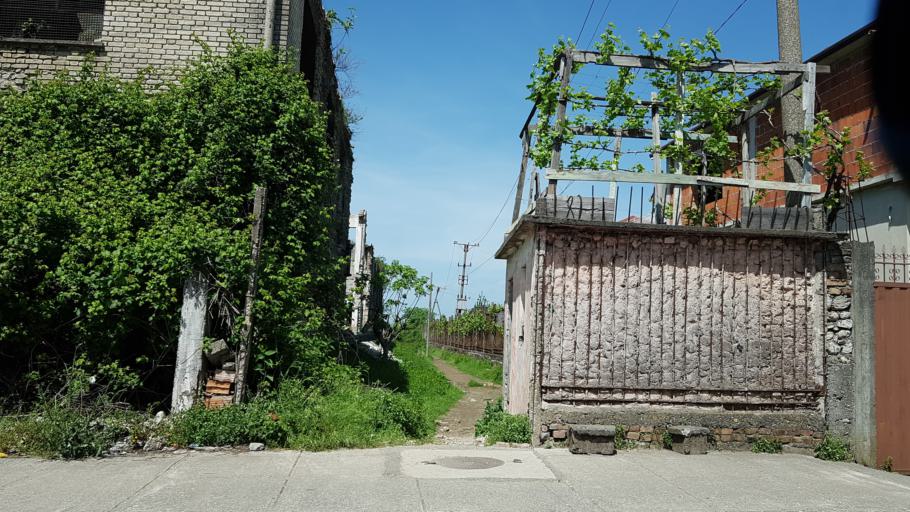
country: AL
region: Shkoder
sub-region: Rrethi i Shkodres
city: Shkoder
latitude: 42.0874
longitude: 19.5313
